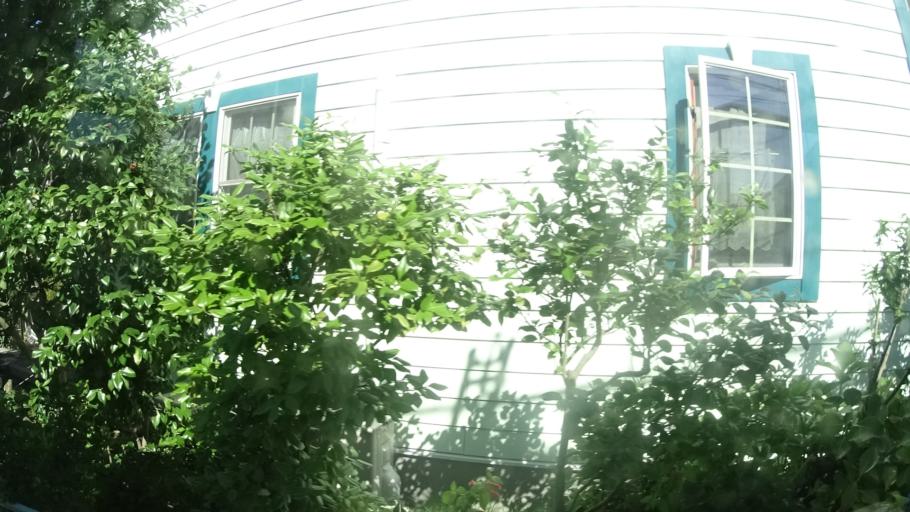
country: JP
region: Kanagawa
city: Fujisawa
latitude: 35.3216
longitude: 139.4826
